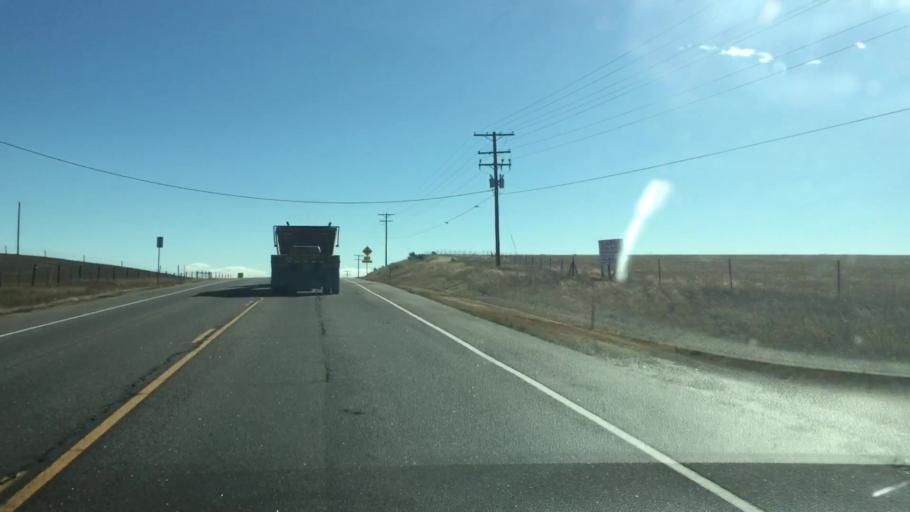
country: US
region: Colorado
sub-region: Elbert County
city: Ponderosa Park
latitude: 39.3620
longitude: -104.6604
